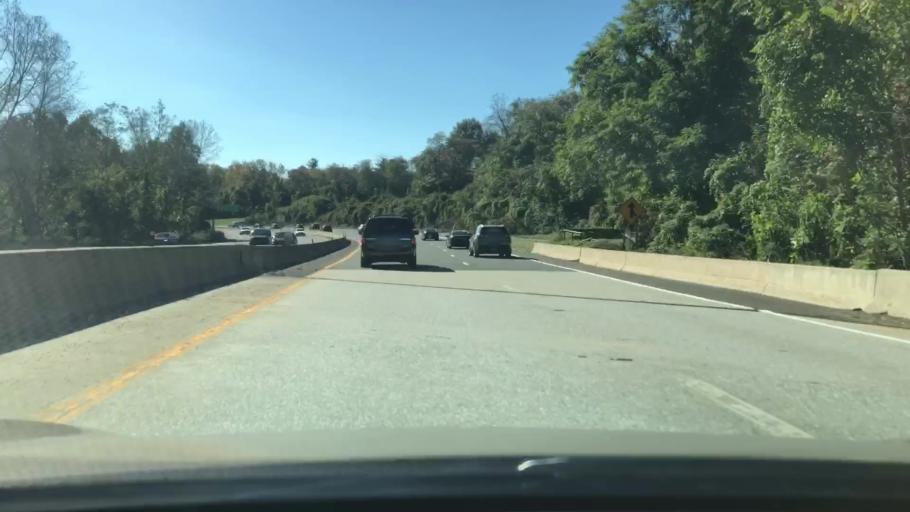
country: US
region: New York
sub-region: Westchester County
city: Tuckahoe
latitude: 40.9438
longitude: -73.8021
